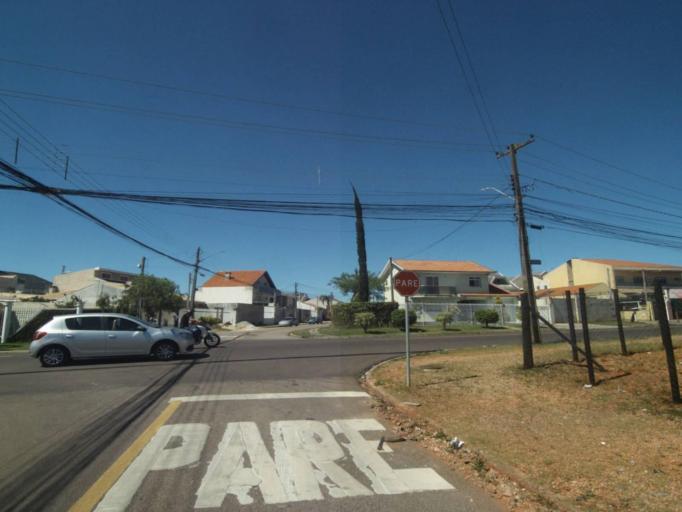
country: BR
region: Parana
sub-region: Curitiba
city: Curitiba
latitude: -25.4814
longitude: -49.3392
